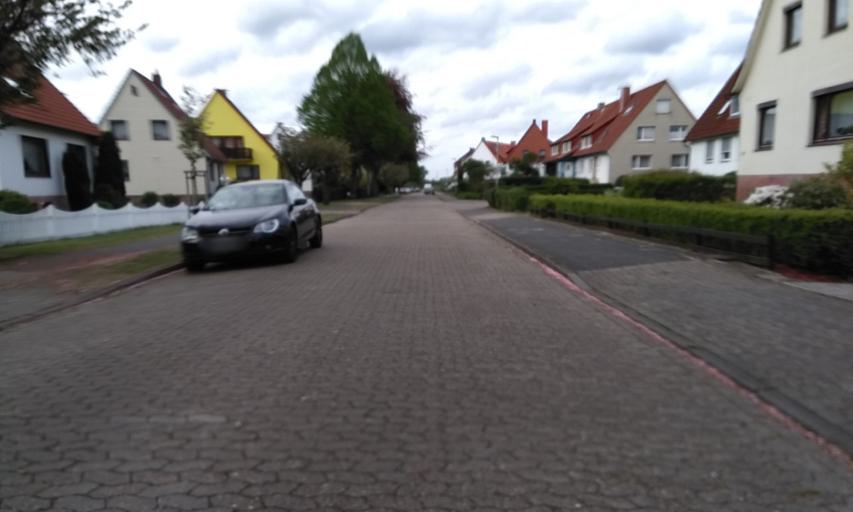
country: DE
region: Lower Saxony
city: Buxtehude
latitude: 53.4739
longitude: 9.6804
